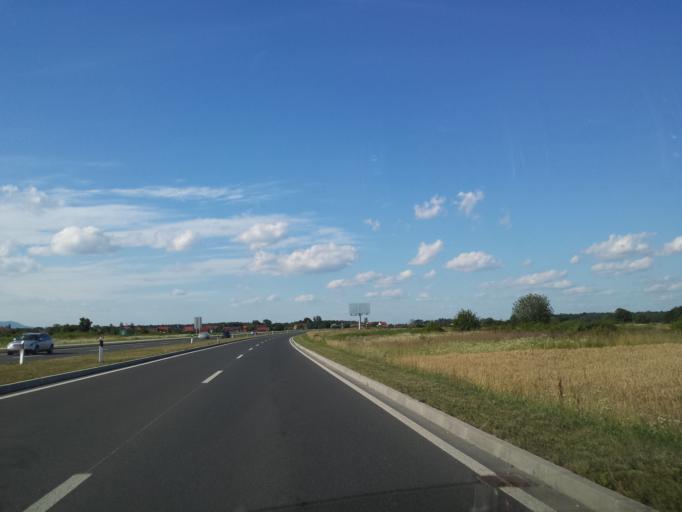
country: HR
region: Zagrebacka
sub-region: Grad Velika Gorica
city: Velika Gorica
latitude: 45.7198
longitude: 16.0882
